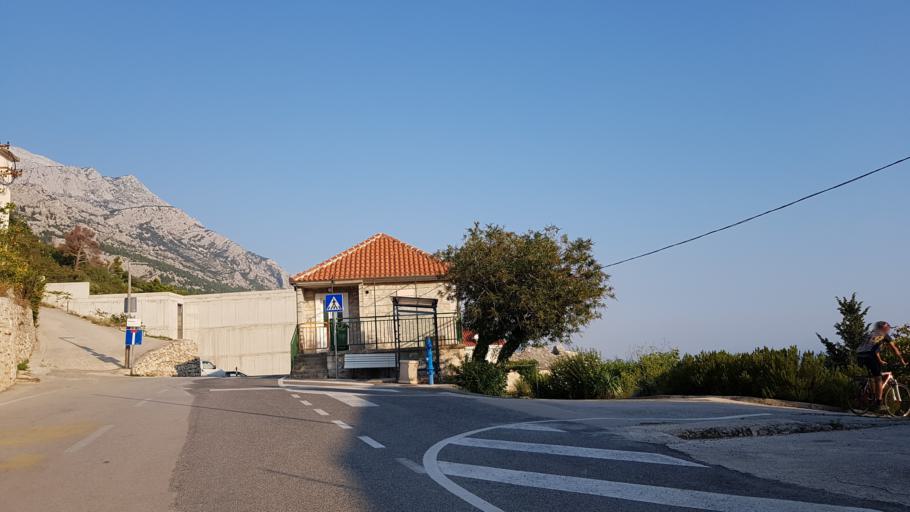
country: HR
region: Splitsko-Dalmatinska
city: Donja Brela
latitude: 43.3843
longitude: 16.9081
